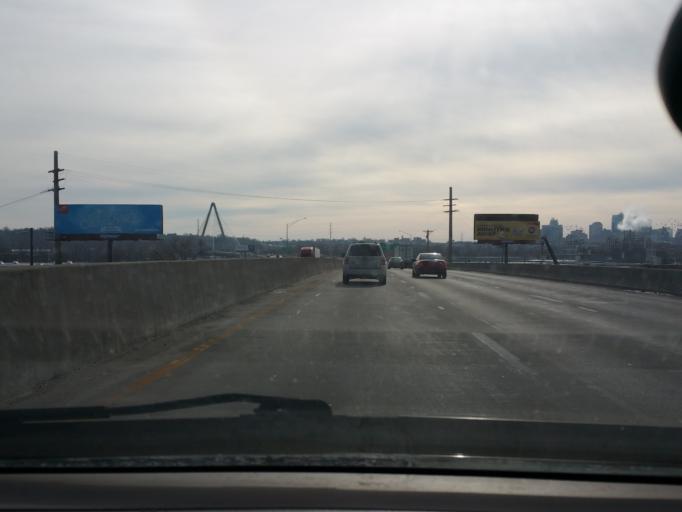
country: US
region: Missouri
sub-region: Clay County
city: North Kansas City
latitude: 39.1327
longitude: -94.5680
